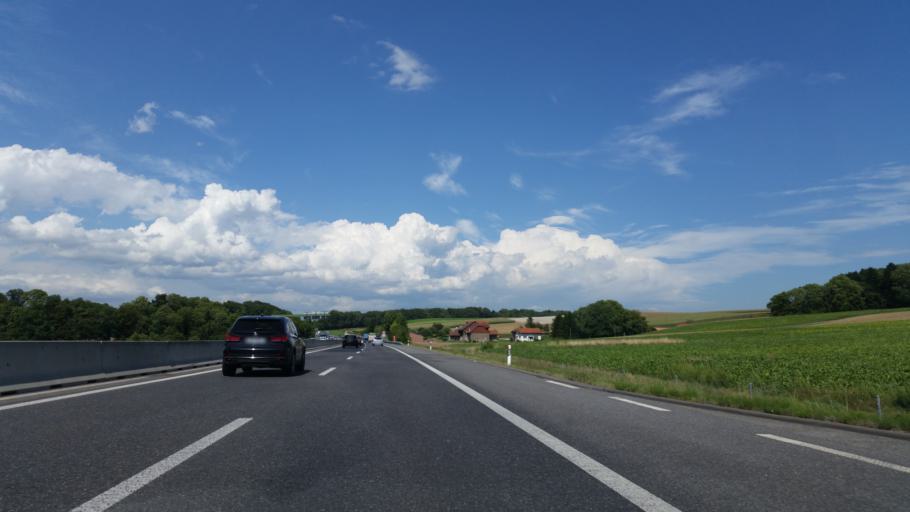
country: CH
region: Vaud
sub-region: Gros-de-Vaud District
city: Penthalaz
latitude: 46.6150
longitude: 6.5580
